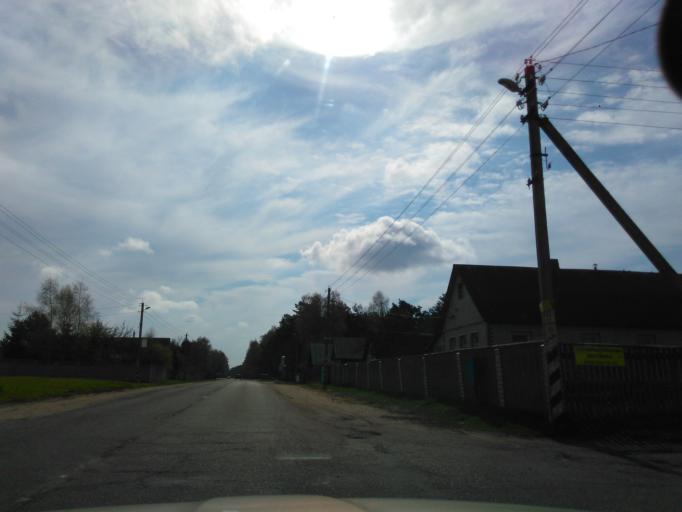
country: BY
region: Minsk
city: Rakaw
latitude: 53.9669
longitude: 27.0667
